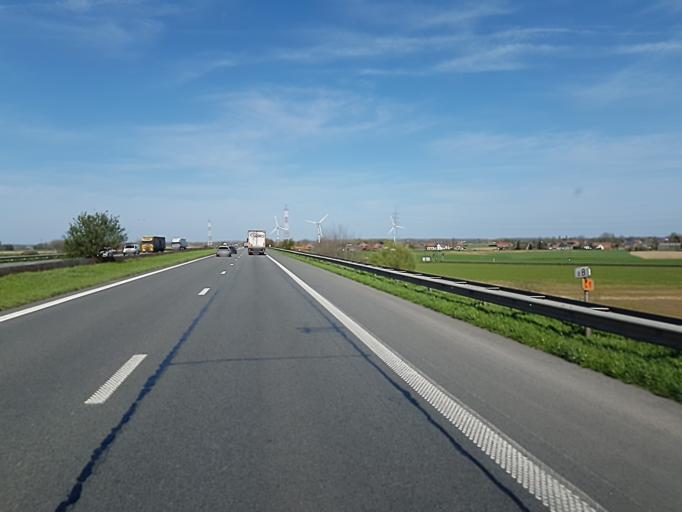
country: BE
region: Wallonia
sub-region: Province du Hainaut
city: Estaimpuis
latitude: 50.6736
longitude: 3.2898
